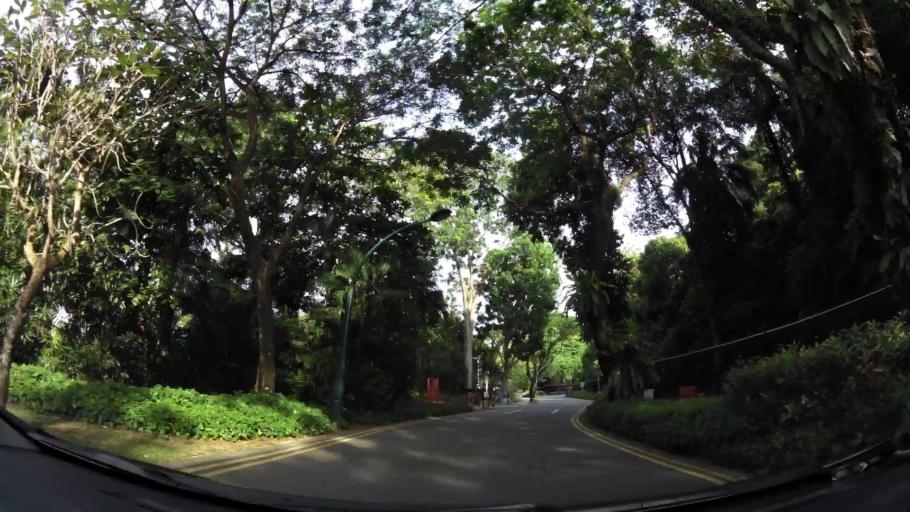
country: SG
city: Singapore
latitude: 1.2463
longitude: 103.8254
